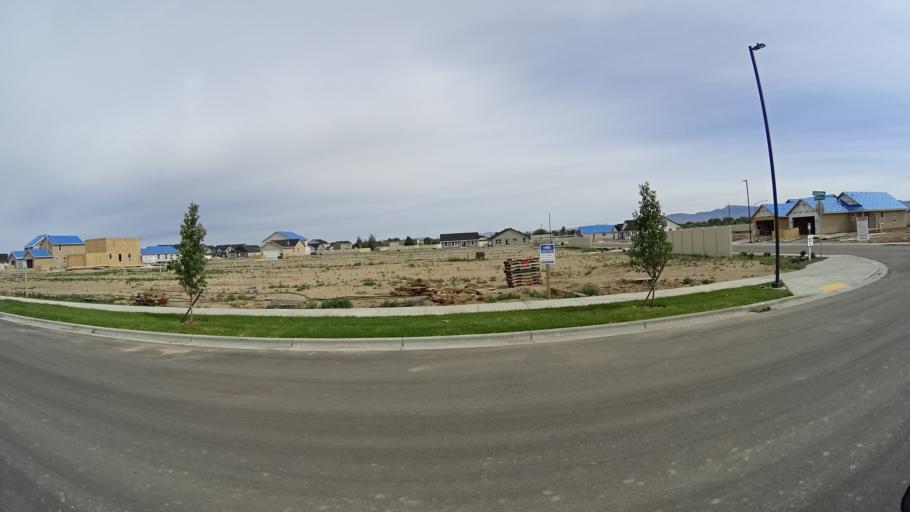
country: US
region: Idaho
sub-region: Ada County
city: Garden City
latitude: 43.5329
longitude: -116.2953
